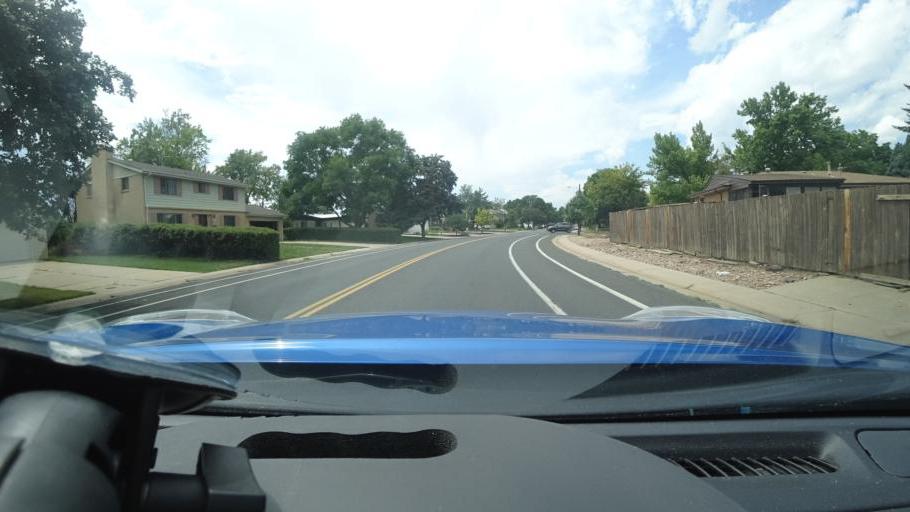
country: US
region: Colorado
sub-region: Adams County
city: Aurora
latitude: 39.7189
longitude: -104.8303
